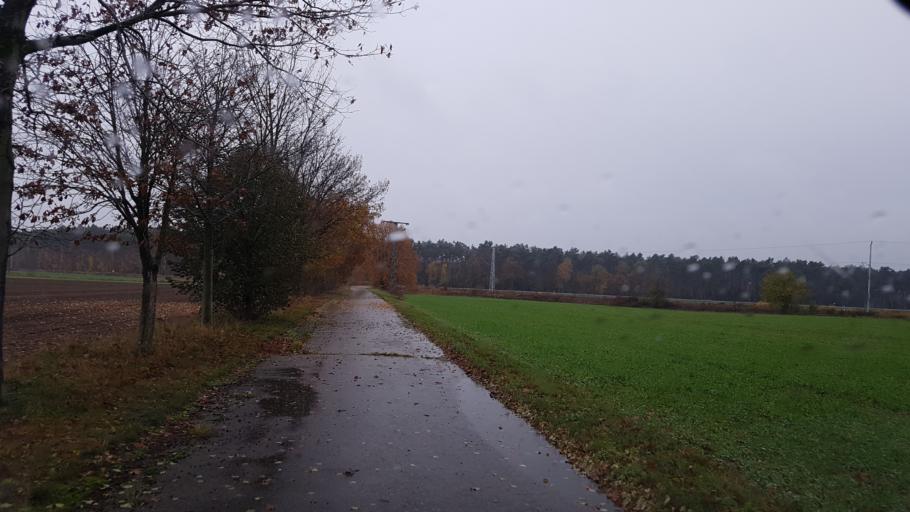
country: DE
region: Brandenburg
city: Herzberg
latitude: 51.6486
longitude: 13.2194
